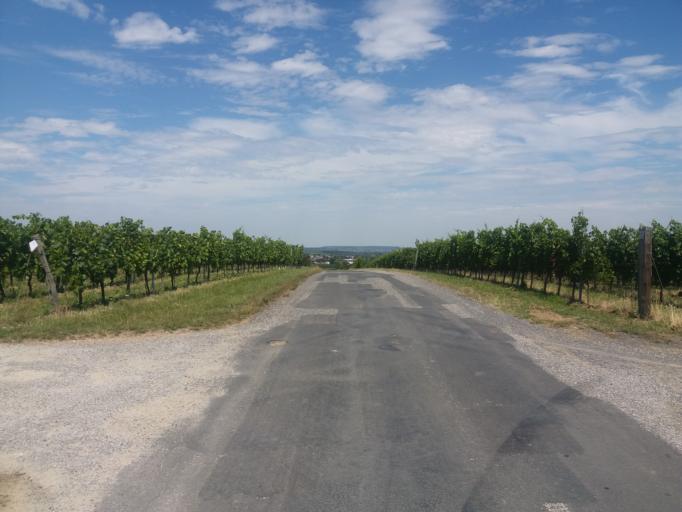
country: AT
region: Burgenland
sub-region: Politischer Bezirk Oberpullendorf
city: Raiding
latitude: 47.5707
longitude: 16.5403
